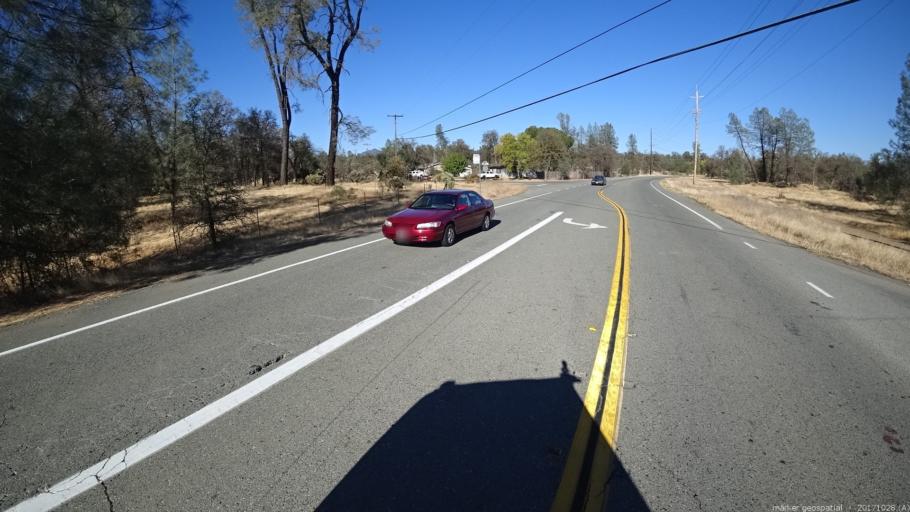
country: US
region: California
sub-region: Shasta County
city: Central Valley (historical)
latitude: 40.6404
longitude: -122.3752
